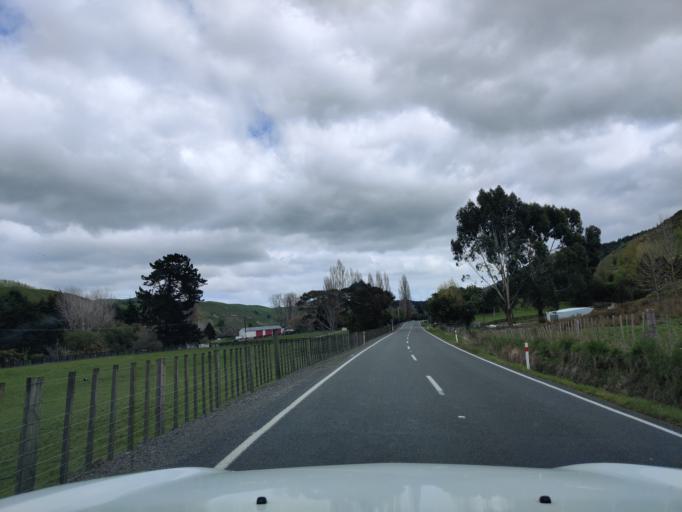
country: NZ
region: Manawatu-Wanganui
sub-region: Wanganui District
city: Wanganui
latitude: -39.8436
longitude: 175.1533
